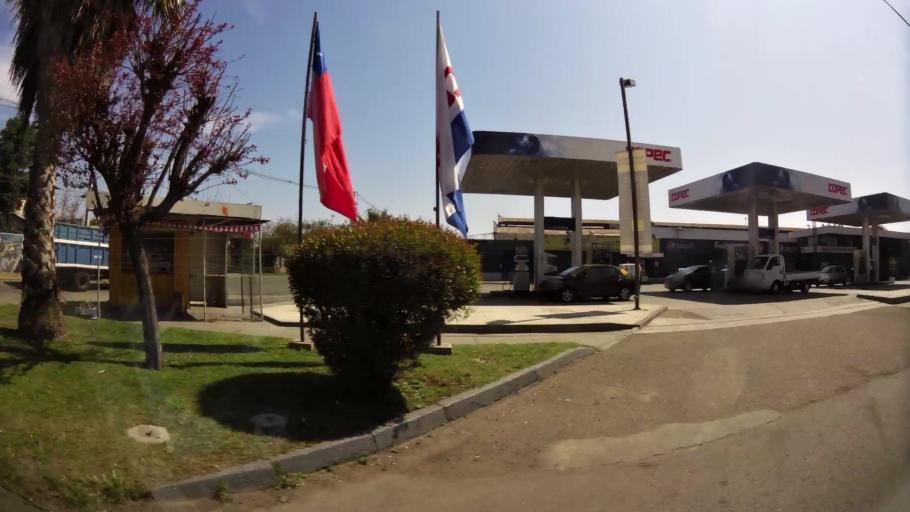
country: CL
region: Santiago Metropolitan
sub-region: Provincia de Santiago
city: Lo Prado
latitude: -33.4709
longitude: -70.7188
